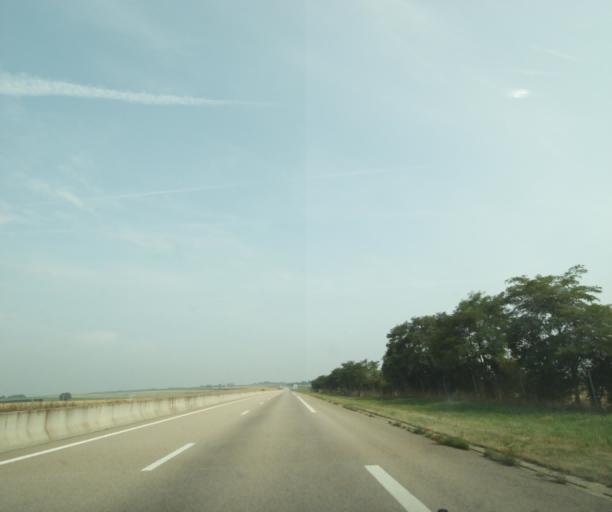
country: FR
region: Lower Normandy
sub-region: Departement de l'Orne
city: Courteilles
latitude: 48.7939
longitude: -0.1267
